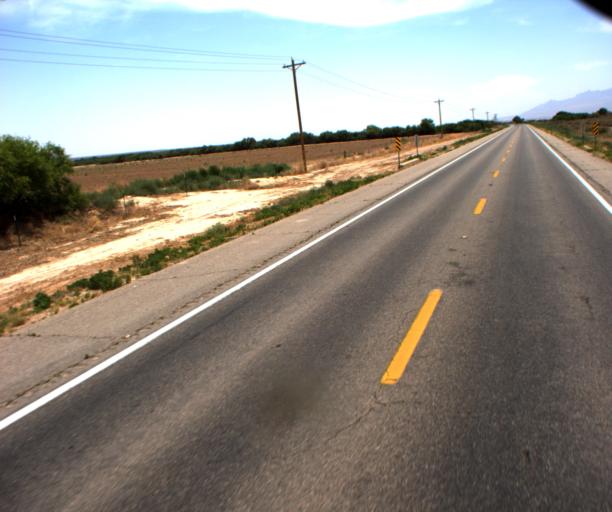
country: US
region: Arizona
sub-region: Graham County
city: Pima
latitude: 32.9969
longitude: -109.9411
